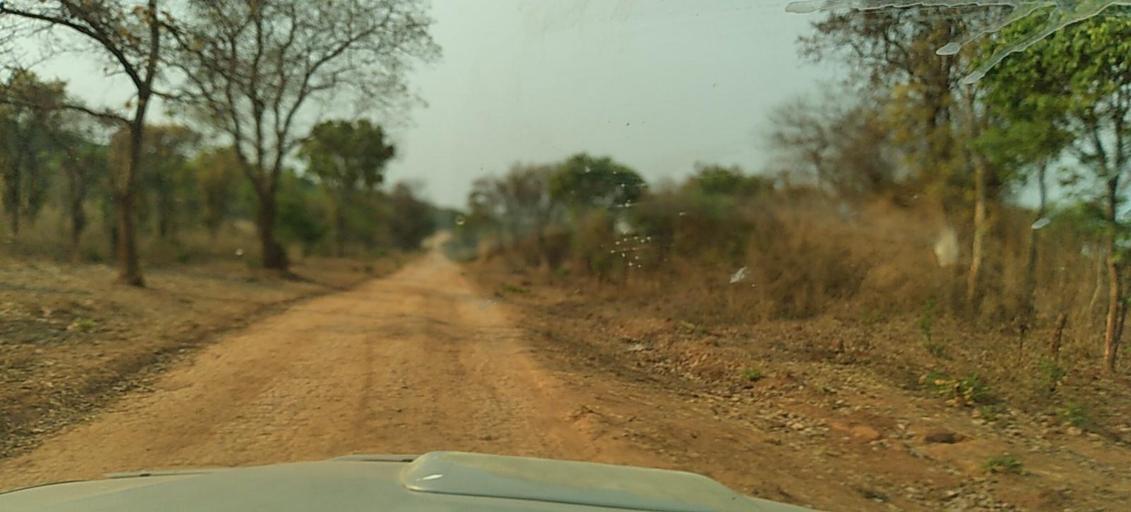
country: ZM
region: North-Western
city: Kasempa
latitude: -13.2850
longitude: 26.5550
